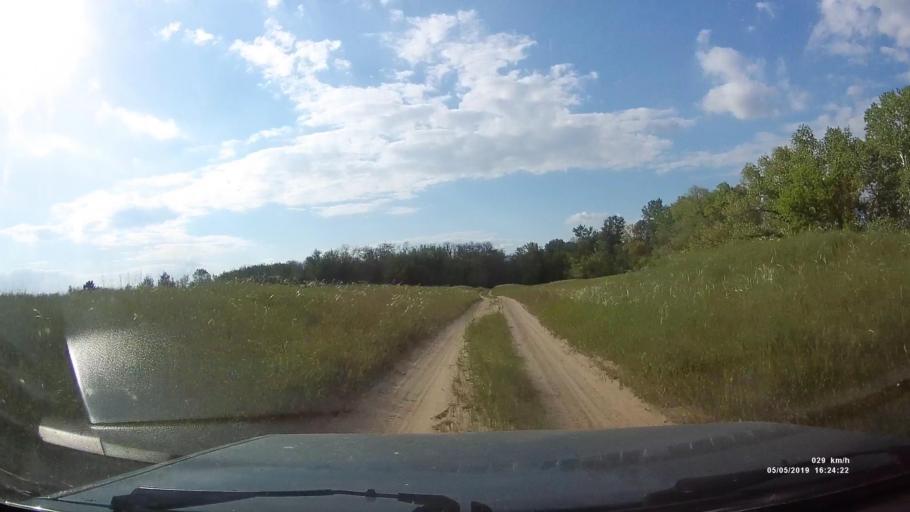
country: RU
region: Rostov
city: Konstantinovsk
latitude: 47.7591
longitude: 41.0264
